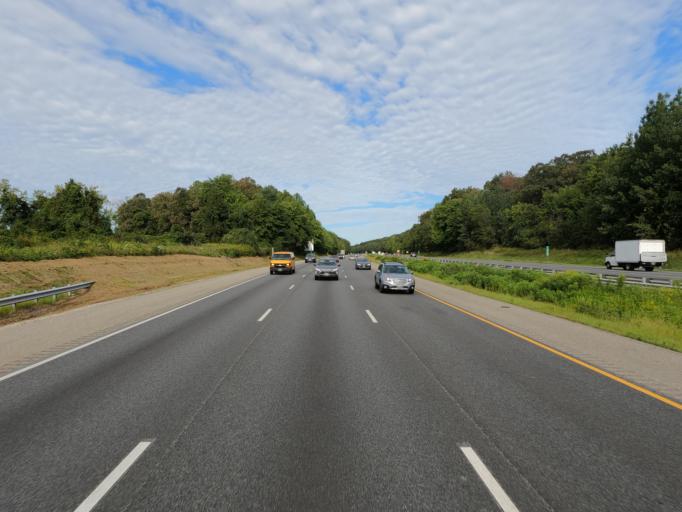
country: US
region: Maryland
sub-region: Cecil County
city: Elkton
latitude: 39.6432
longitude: -75.8289
